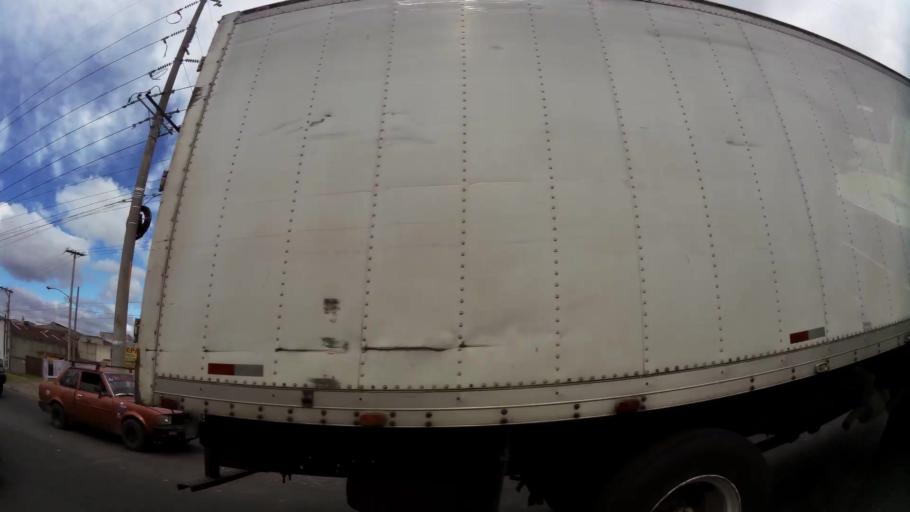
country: GT
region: Guatemala
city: Guatemala City
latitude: 14.6055
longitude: -90.5337
